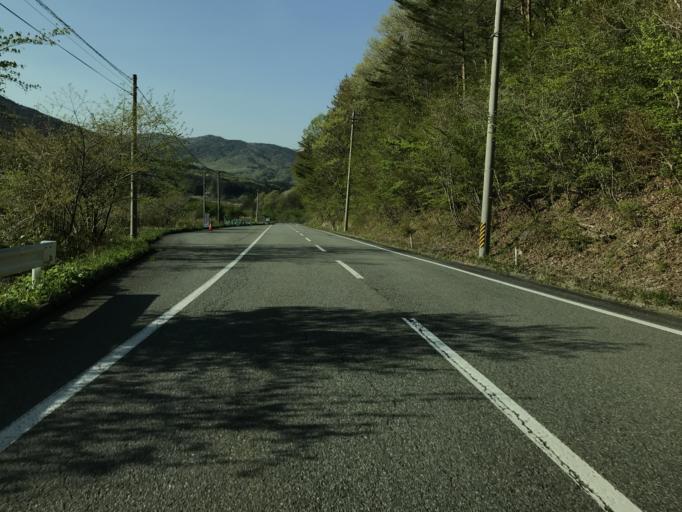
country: JP
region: Fukushima
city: Funehikimachi-funehiki
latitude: 37.5456
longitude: 140.7369
